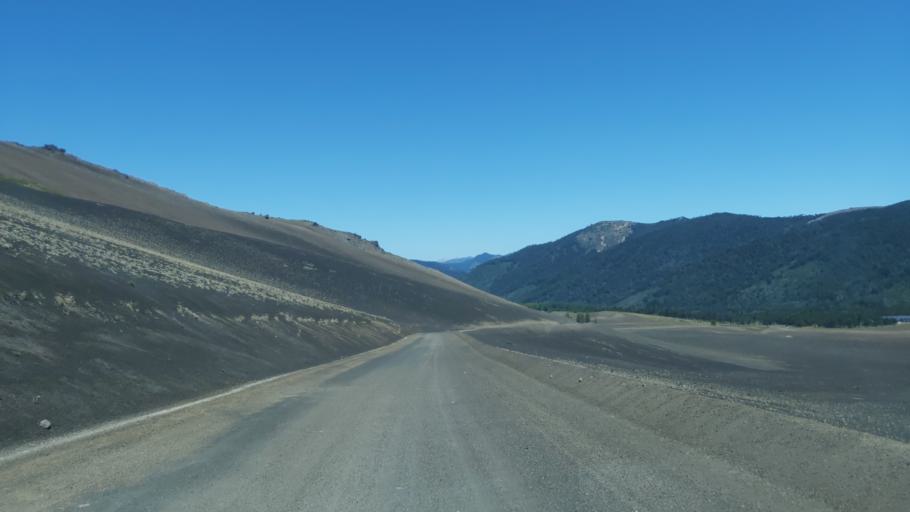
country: CL
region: Araucania
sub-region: Provincia de Cautin
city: Vilcun
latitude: -38.4064
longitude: -71.5429
